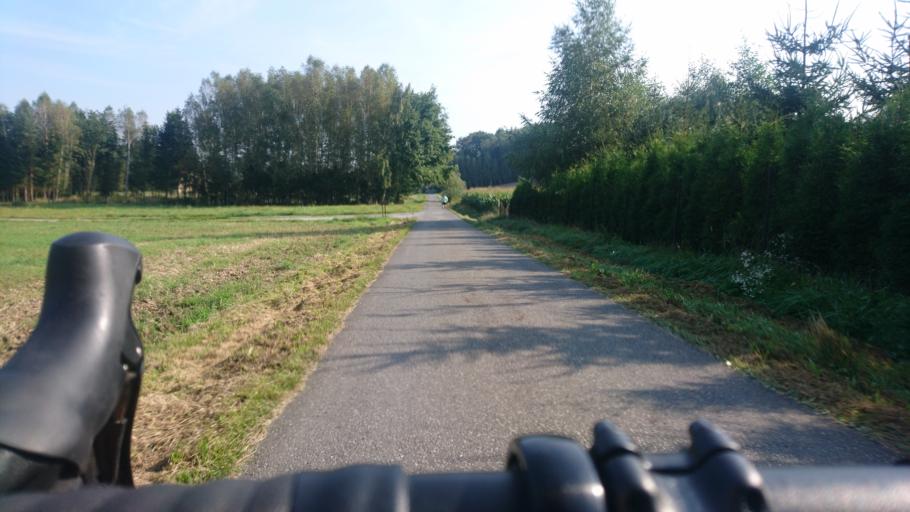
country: PL
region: Lesser Poland Voivodeship
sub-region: Powiat wadowicki
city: Sosnowice
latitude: 49.9540
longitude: 19.7048
